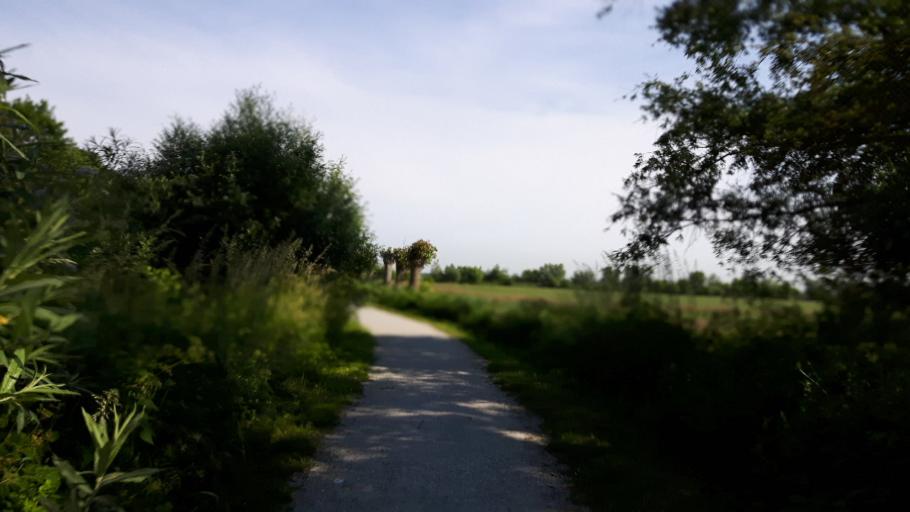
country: NL
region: Utrecht
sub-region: Stichtse Vecht
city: Breukelen
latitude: 52.1792
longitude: 4.9538
